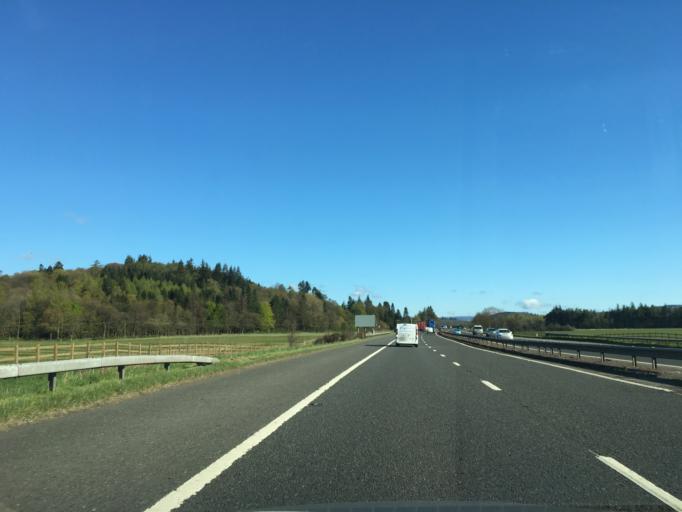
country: GB
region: Scotland
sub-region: Stirling
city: Stirling
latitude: 56.1245
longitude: -3.9709
